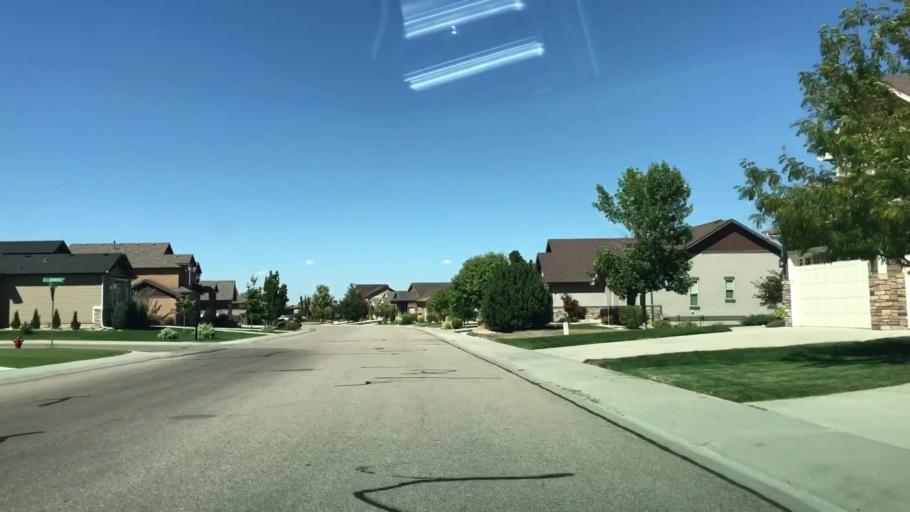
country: US
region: Colorado
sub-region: Weld County
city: Windsor
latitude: 40.4529
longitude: -104.9488
